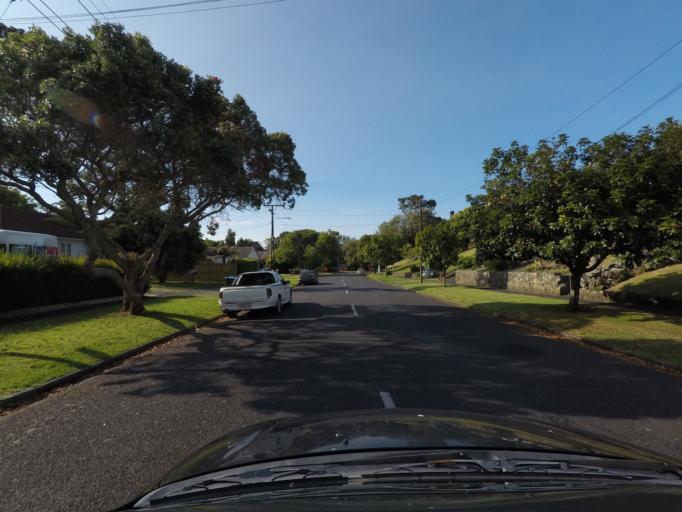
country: NZ
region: Auckland
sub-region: Auckland
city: Auckland
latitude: -36.9052
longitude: 174.7509
